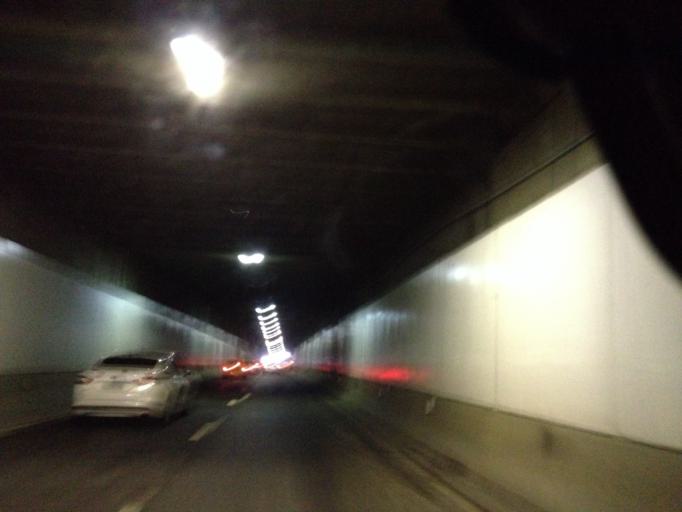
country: BR
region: Rio de Janeiro
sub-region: Rio De Janeiro
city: Rio de Janeiro
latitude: -23.0119
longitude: -43.2912
